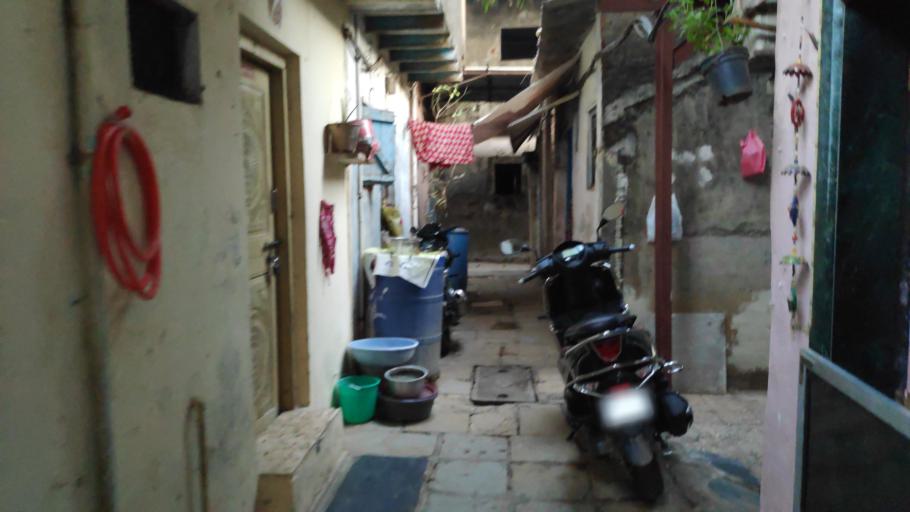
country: IN
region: Maharashtra
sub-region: Mumbai Suburban
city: Mumbai
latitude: 19.0764
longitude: 72.8484
